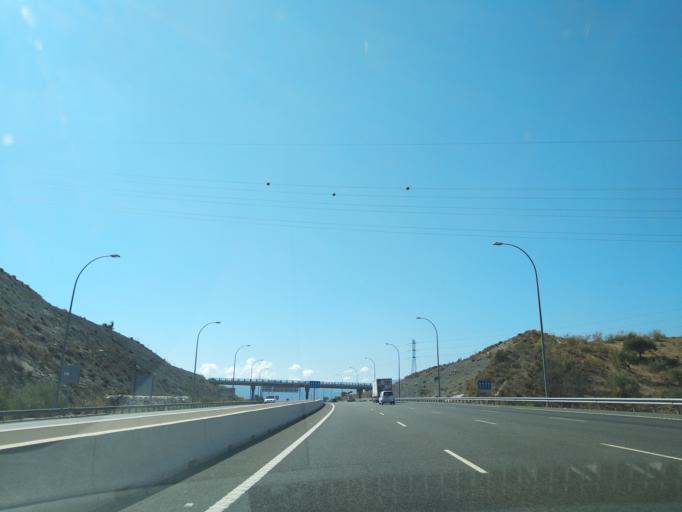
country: ES
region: Andalusia
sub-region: Provincia de Malaga
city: Malaga
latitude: 36.7448
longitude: -4.5015
